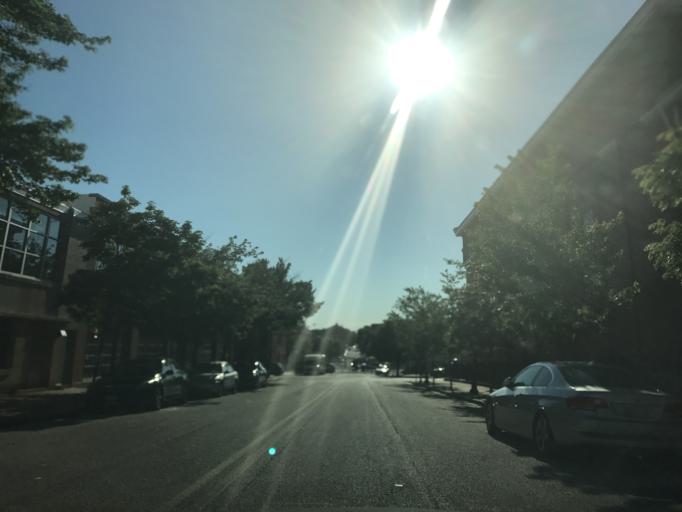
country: US
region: Maryland
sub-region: City of Baltimore
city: Baltimore
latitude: 39.2879
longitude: -76.6313
